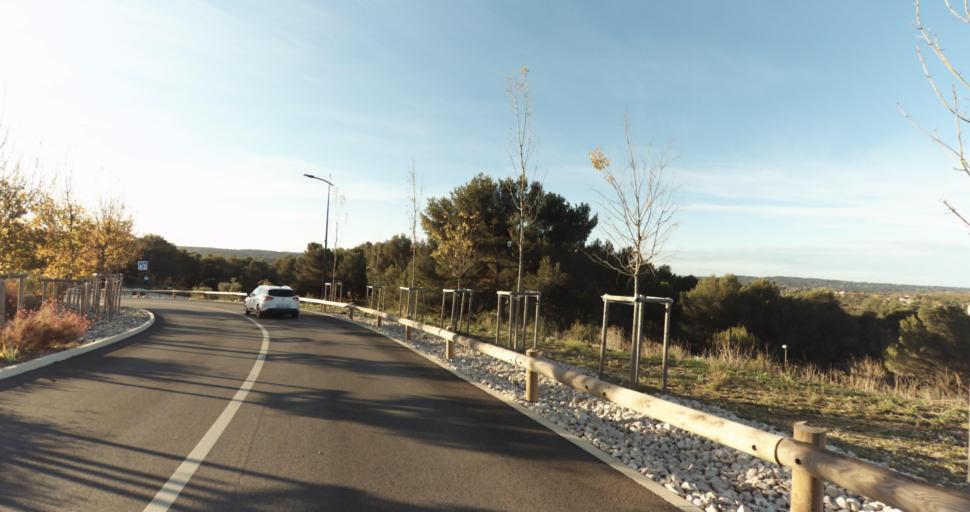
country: FR
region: Provence-Alpes-Cote d'Azur
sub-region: Departement des Bouches-du-Rhone
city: Venelles
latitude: 43.5960
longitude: 5.4917
